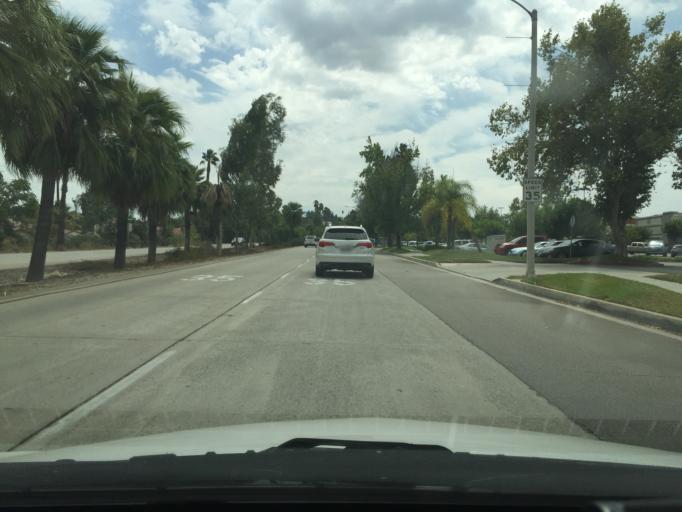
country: US
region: California
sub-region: San Bernardino County
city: Redlands
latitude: 34.0499
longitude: -117.1710
